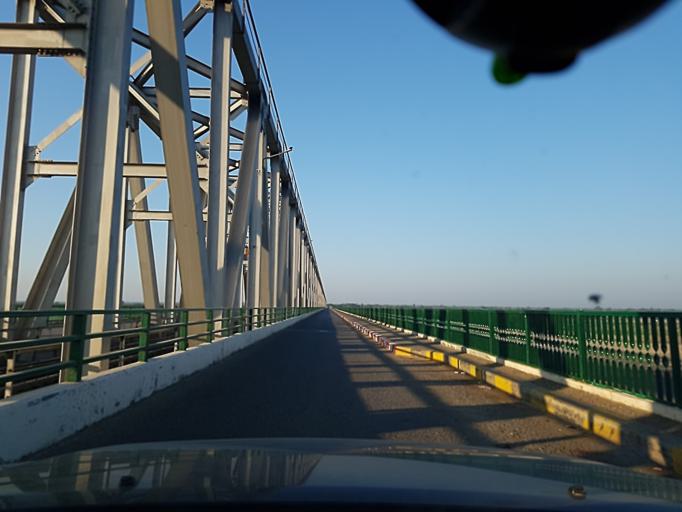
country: MM
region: Sagain
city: Monywa
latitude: 21.8090
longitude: 95.1786
